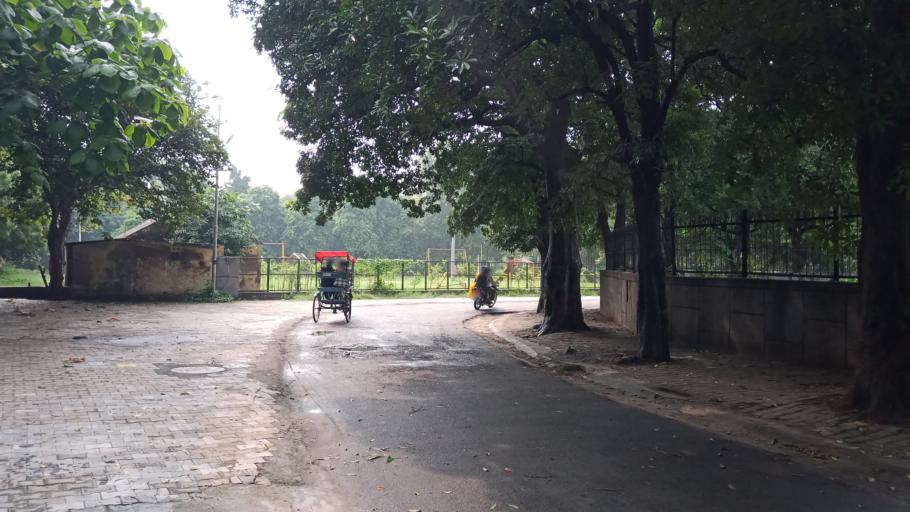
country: IN
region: NCT
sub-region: New Delhi
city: New Delhi
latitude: 28.5759
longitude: 77.2485
